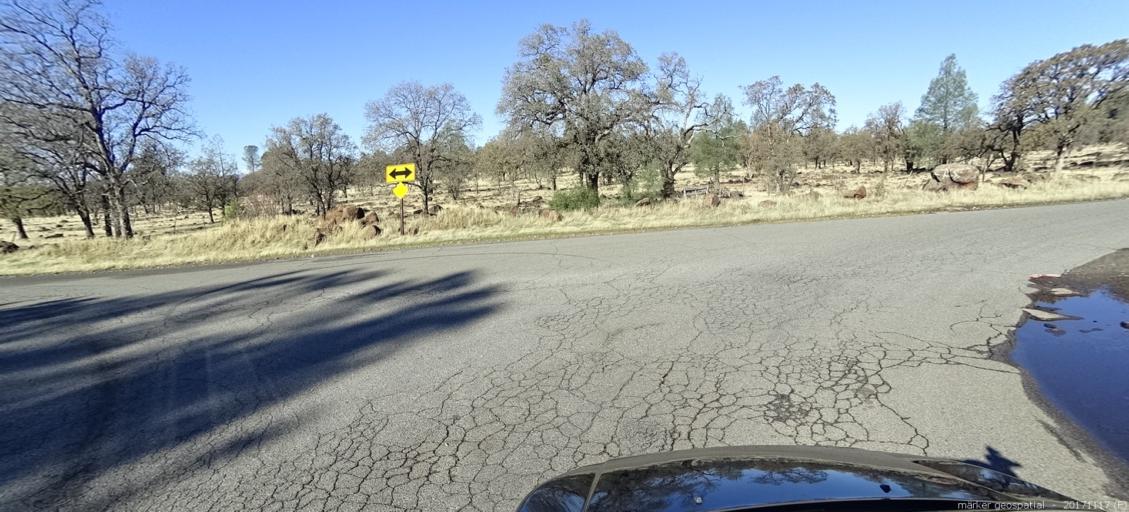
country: US
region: California
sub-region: Shasta County
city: Palo Cedro
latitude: 40.4644
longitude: -122.0976
